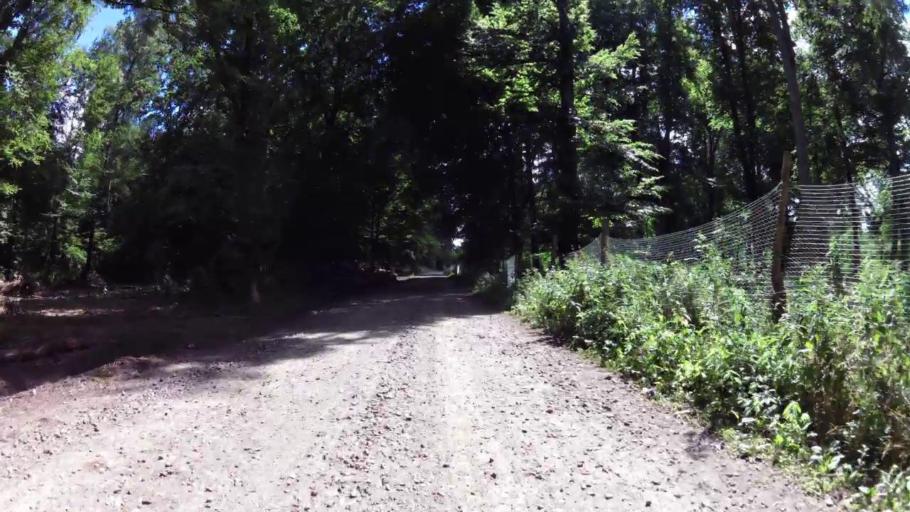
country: PL
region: West Pomeranian Voivodeship
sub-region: Powiat lobeski
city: Radowo Male
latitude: 53.7261
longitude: 15.5334
